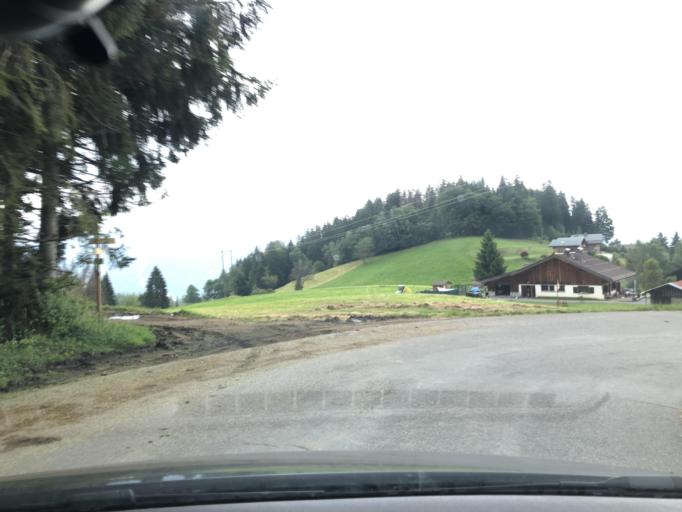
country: FR
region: Rhone-Alpes
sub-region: Departement de la Haute-Savoie
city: Combloux
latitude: 45.9028
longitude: 6.6190
